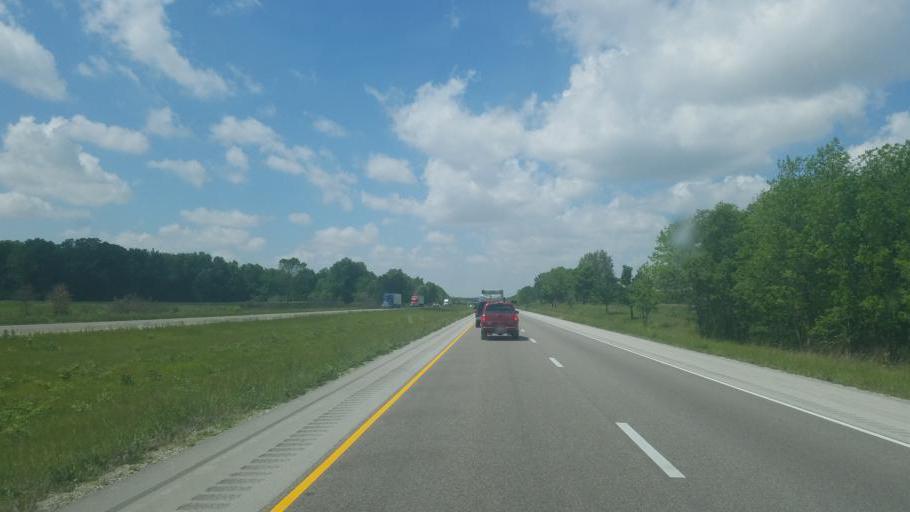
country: US
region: Illinois
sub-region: Cumberland County
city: Toledo
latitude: 39.2224
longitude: -88.2358
